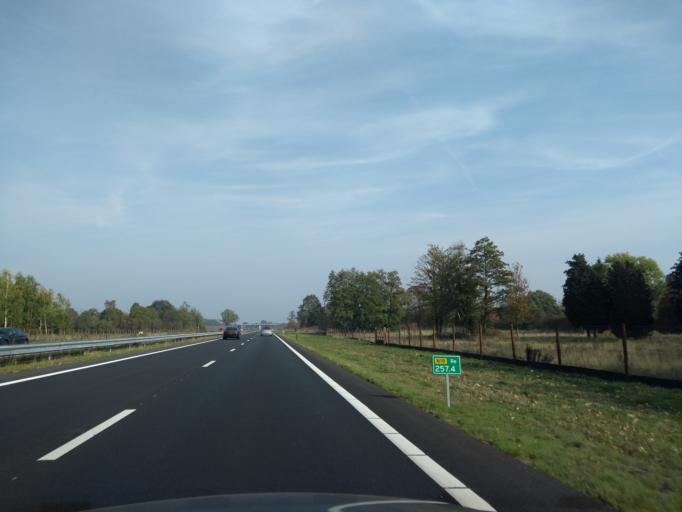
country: NL
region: Overijssel
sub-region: Gemeente Haaksbergen
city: Haaksbergen
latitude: 52.1832
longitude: 6.8025
